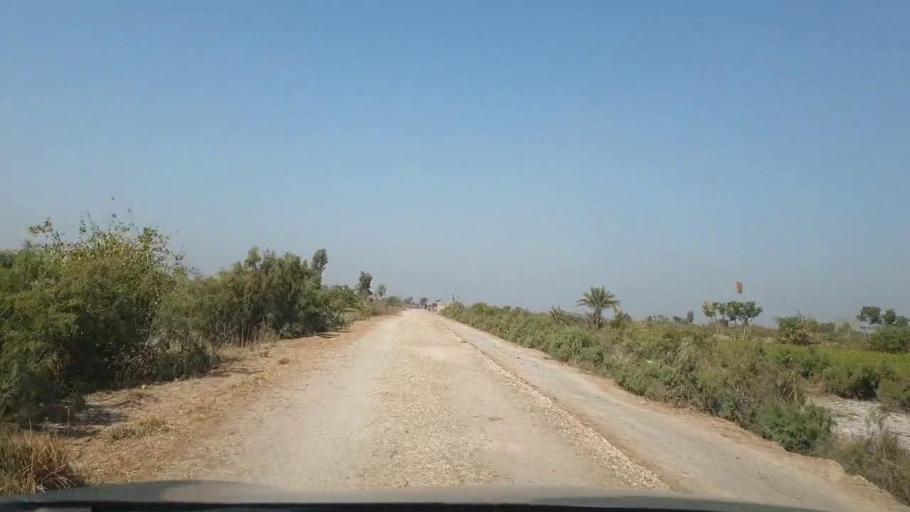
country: PK
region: Sindh
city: Berani
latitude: 25.6823
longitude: 68.8922
